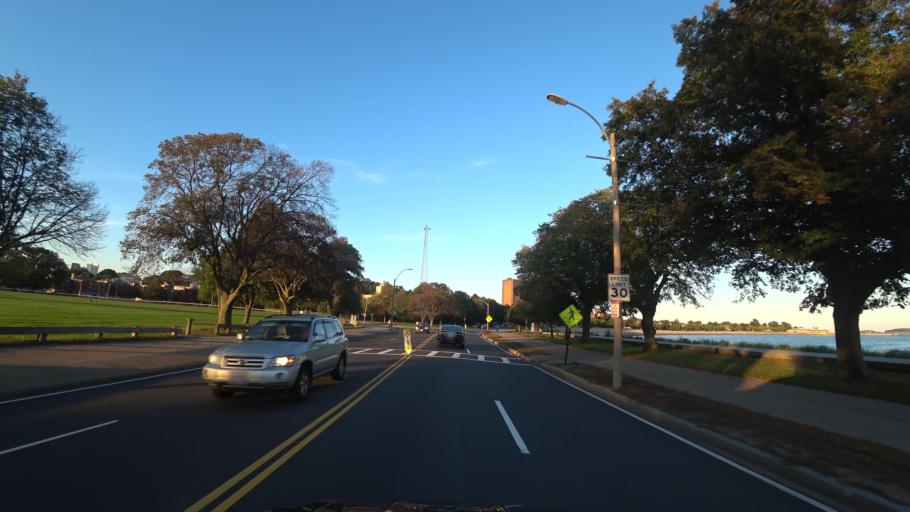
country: US
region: Massachusetts
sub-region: Suffolk County
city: South Boston
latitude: 42.3277
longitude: -71.0480
